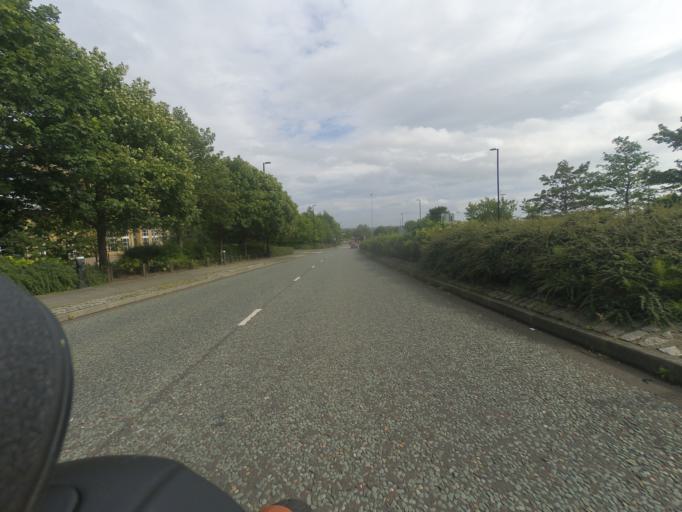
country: GB
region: England
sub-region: South Tyneside
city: Jarrow
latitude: 54.9967
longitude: -1.4665
